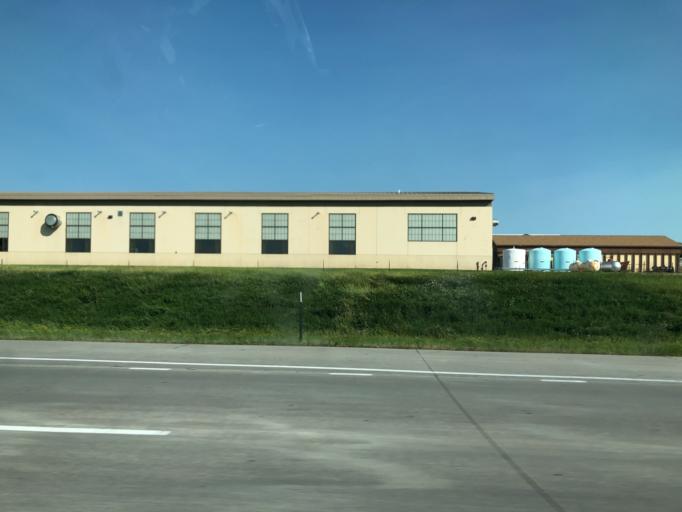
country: US
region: Nebraska
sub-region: Saunders County
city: Ashland
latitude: 40.9677
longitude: -96.3945
